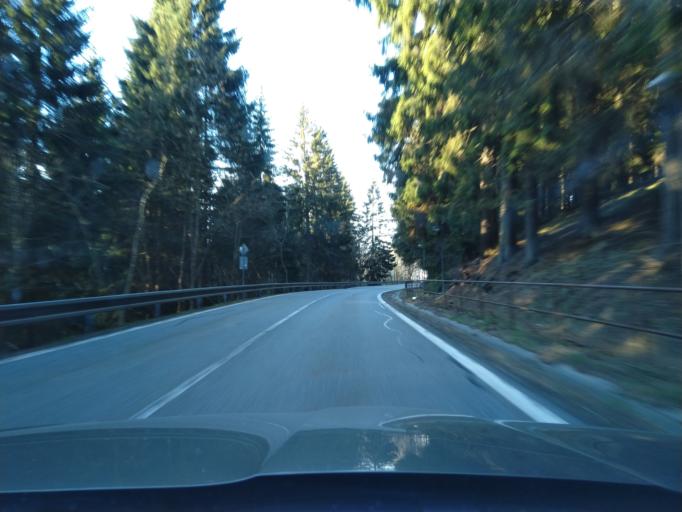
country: CZ
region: Jihocesky
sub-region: Okres Prachatice
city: Vimperk
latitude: 48.9823
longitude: 13.7712
